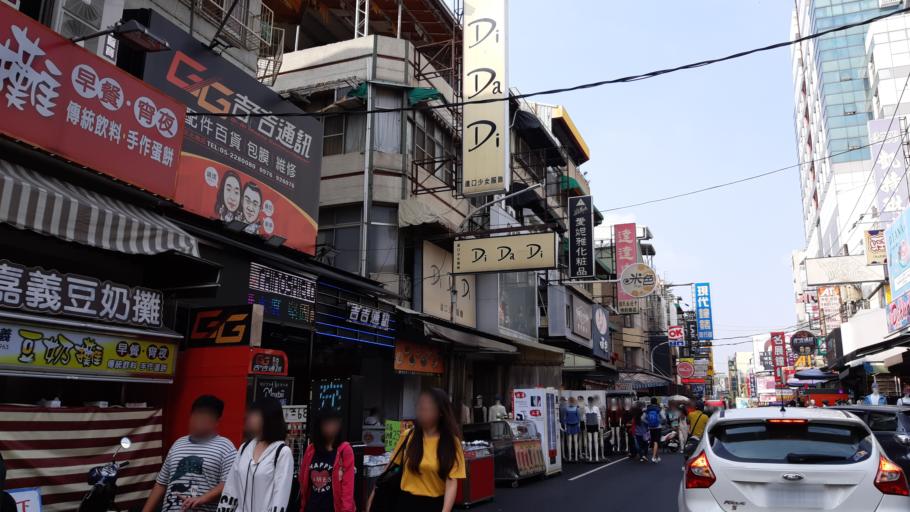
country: TW
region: Taiwan
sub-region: Chiayi
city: Jiayi Shi
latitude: 23.4782
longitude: 120.4499
